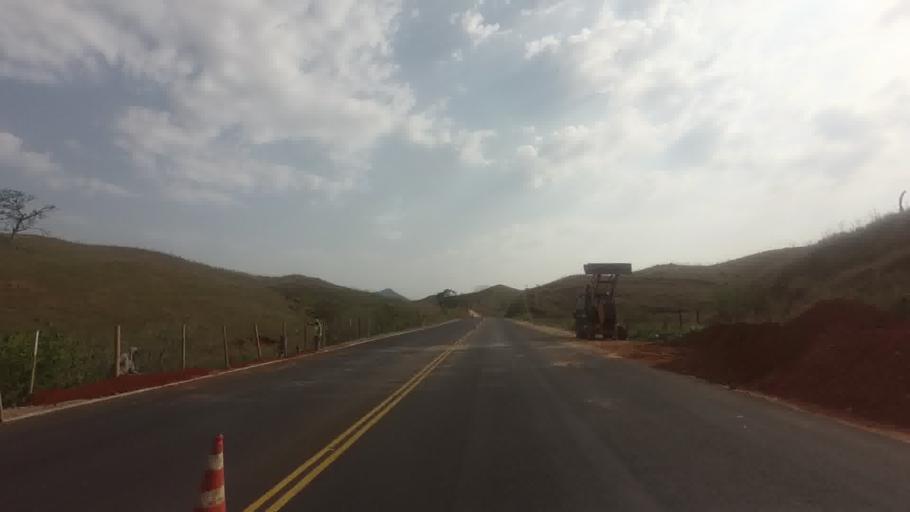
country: BR
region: Rio de Janeiro
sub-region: Itaperuna
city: Itaperuna
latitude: -21.2905
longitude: -41.8035
